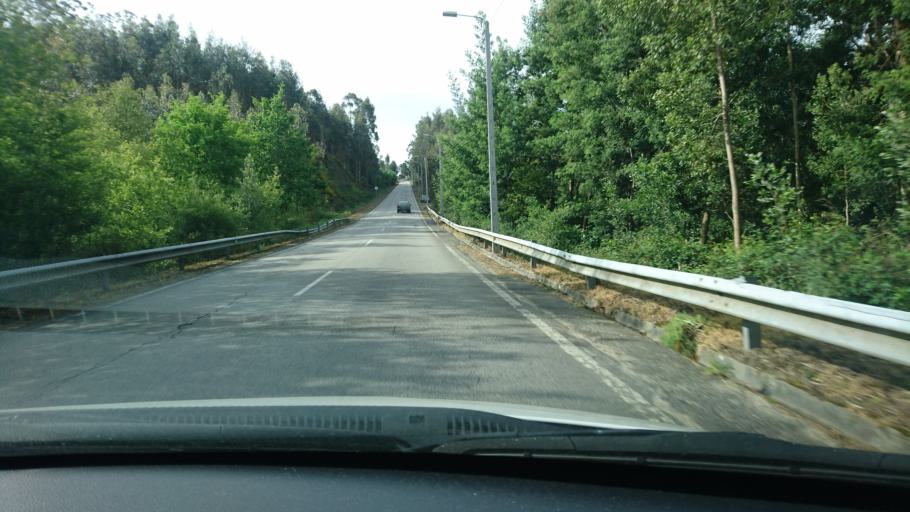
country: PT
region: Aveiro
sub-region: Oliveira de Azemeis
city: Sao Roque
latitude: 40.8678
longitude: -8.4759
